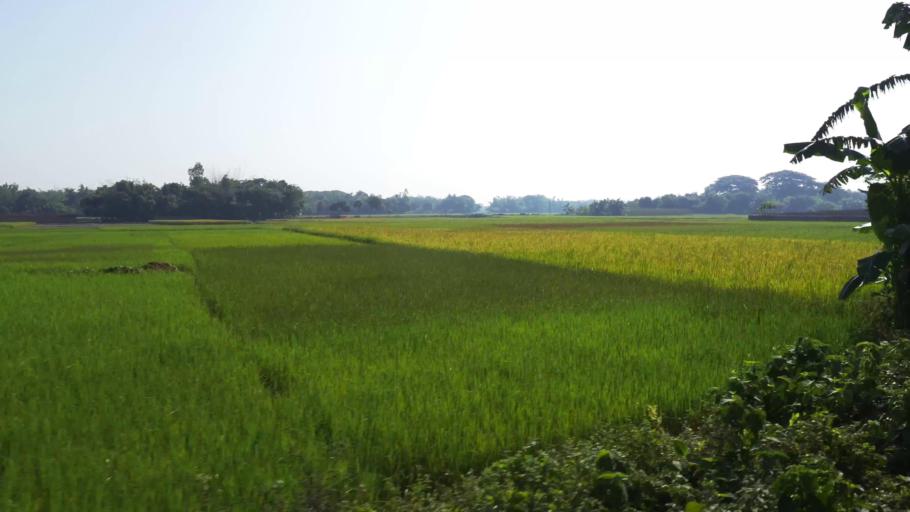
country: BD
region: Dhaka
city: Muktagacha
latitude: 24.7965
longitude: 90.3133
